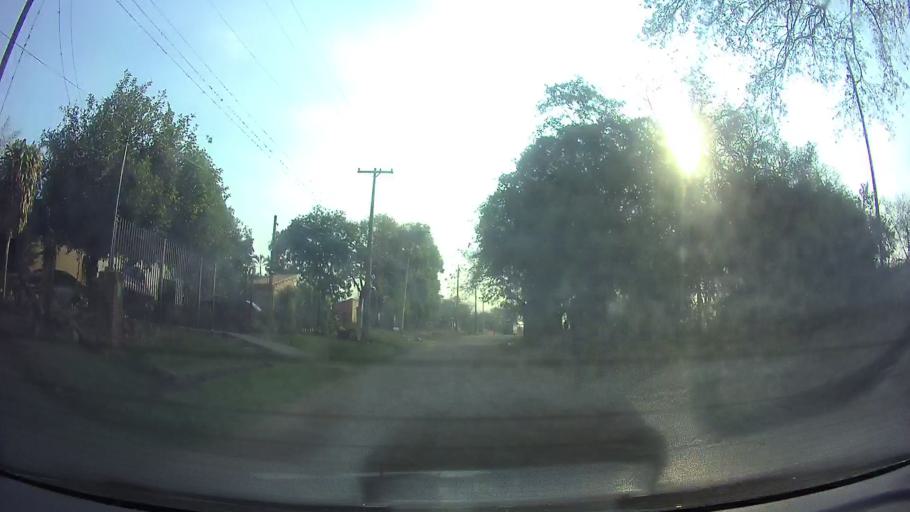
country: PY
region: Central
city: Limpio
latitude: -25.2181
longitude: -57.4966
